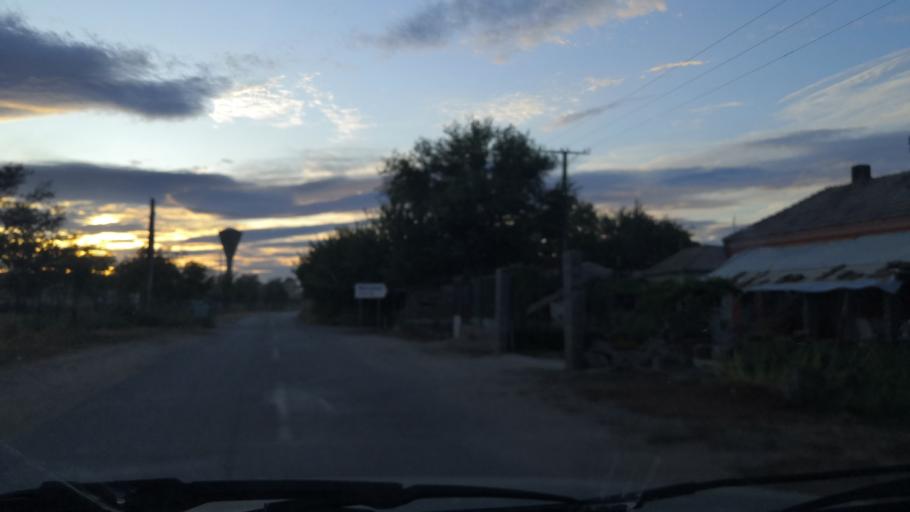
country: RO
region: Mehedinti
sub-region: Comuna Gruia
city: Izvoarele
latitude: 44.2888
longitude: 22.6129
